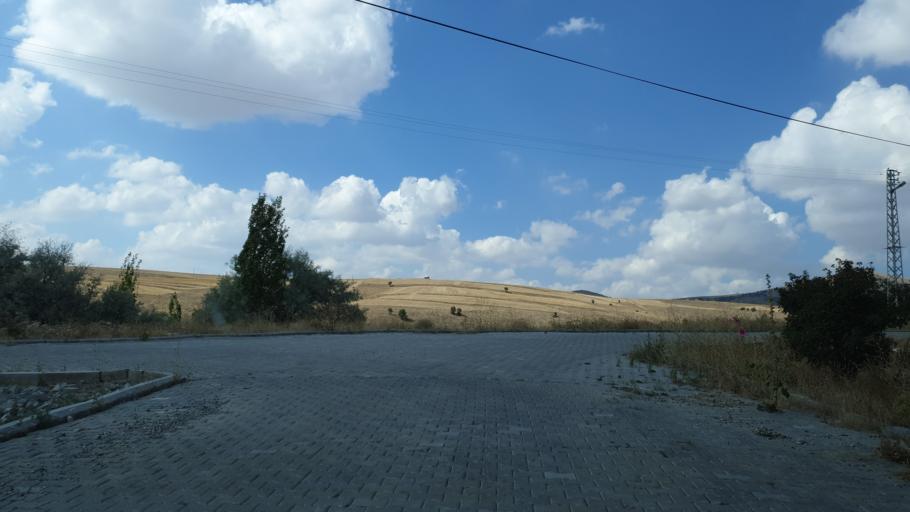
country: TR
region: Kayseri
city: Felahiye
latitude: 39.1175
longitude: 35.6078
